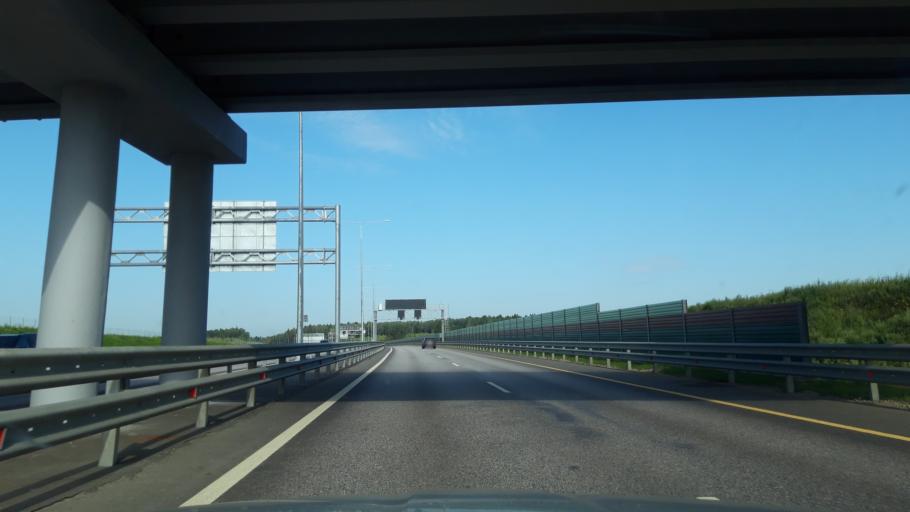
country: RU
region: Moskovskaya
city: Peshki
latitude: 56.1421
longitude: 37.0346
